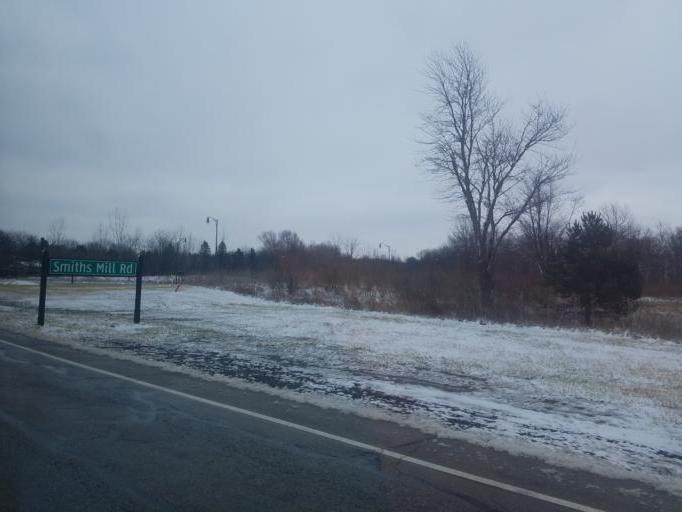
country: US
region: Ohio
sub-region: Franklin County
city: New Albany
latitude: 40.0845
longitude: -82.7879
